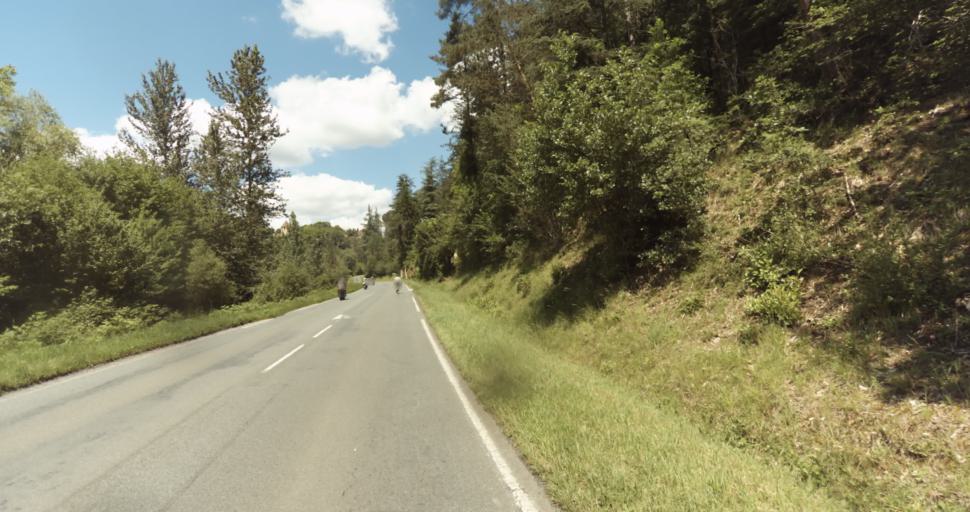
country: FR
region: Aquitaine
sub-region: Departement de la Dordogne
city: Lalinde
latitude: 44.8514
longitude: 0.8110
